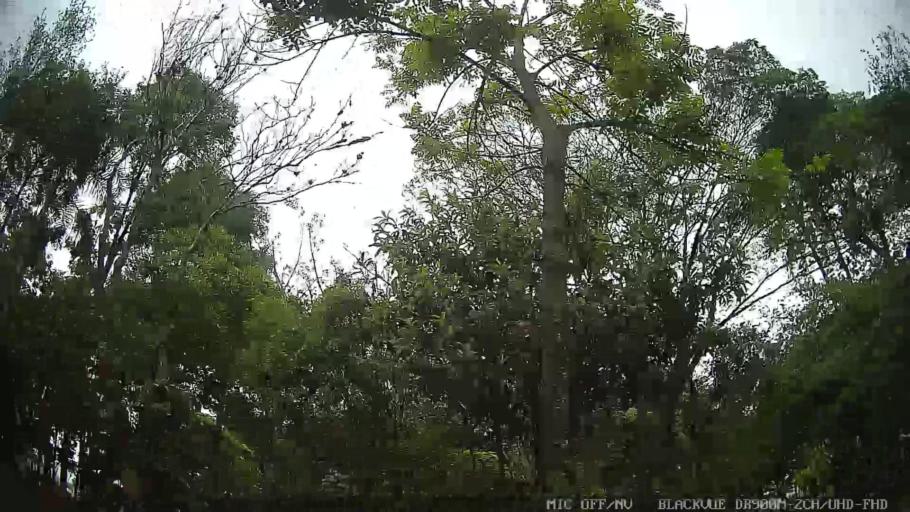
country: BR
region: Sao Paulo
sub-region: Osasco
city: Osasco
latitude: -23.5222
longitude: -46.7192
